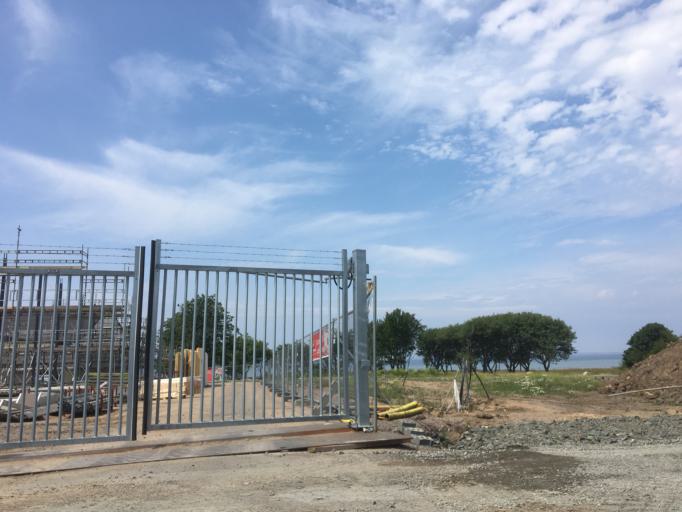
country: SE
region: Skane
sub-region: Landskrona
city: Landskrona
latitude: 55.9016
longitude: 12.8063
